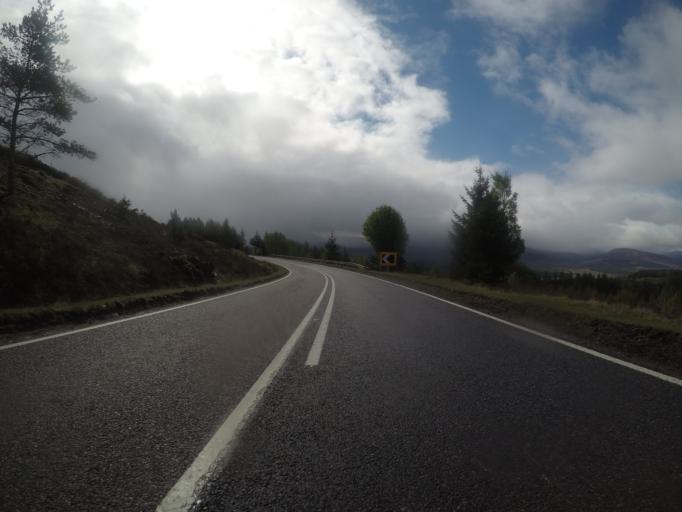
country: GB
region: Scotland
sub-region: Highland
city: Spean Bridge
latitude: 57.0888
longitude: -4.9812
